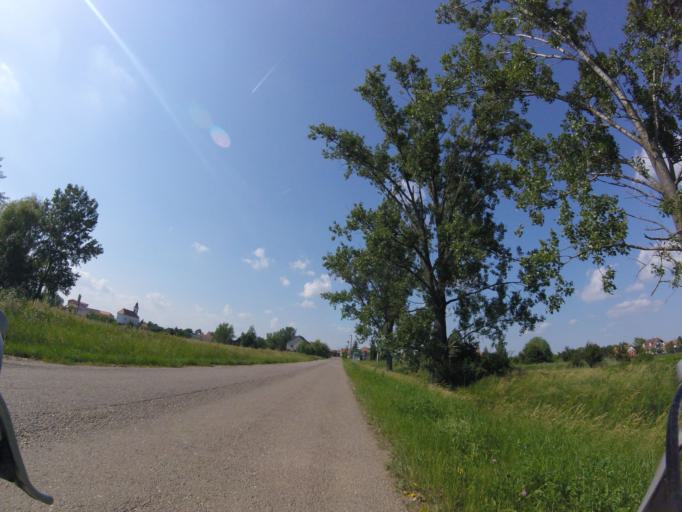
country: HU
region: Heves
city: Kiskore
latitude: 47.4926
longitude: 20.4990
